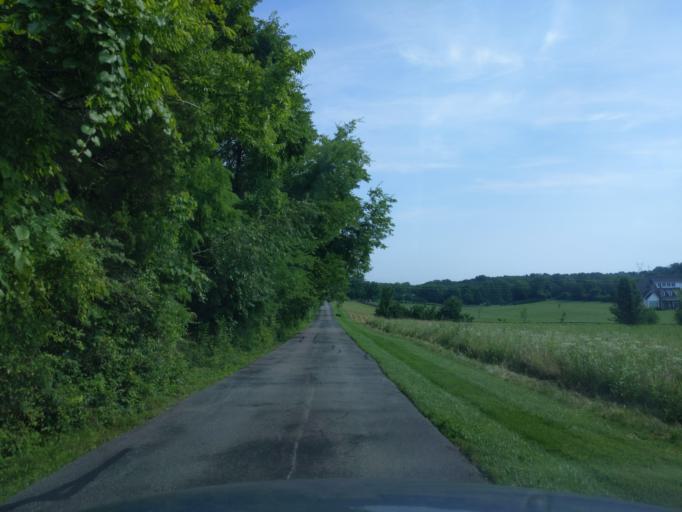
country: US
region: Tennessee
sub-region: Williamson County
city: Brentwood Estates
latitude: 36.0144
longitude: -86.7579
